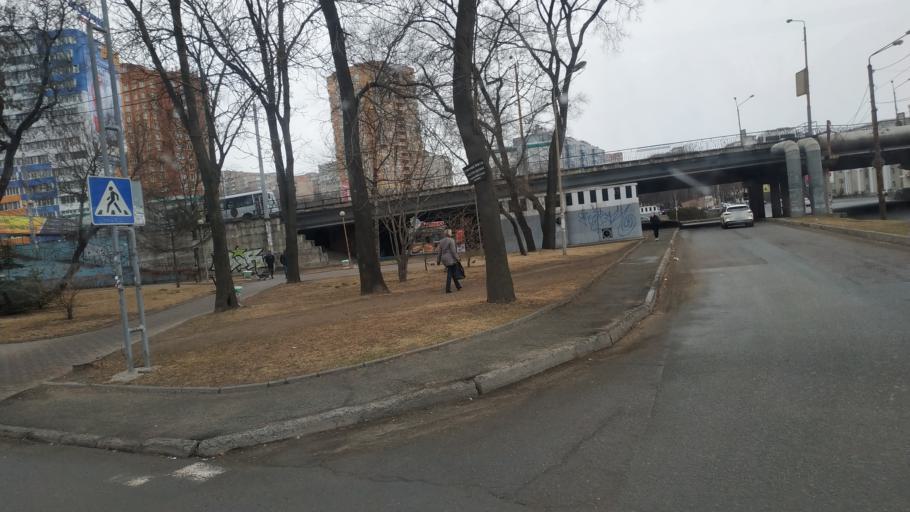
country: RU
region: Primorskiy
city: Vladivostok
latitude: 43.1325
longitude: 131.9124
